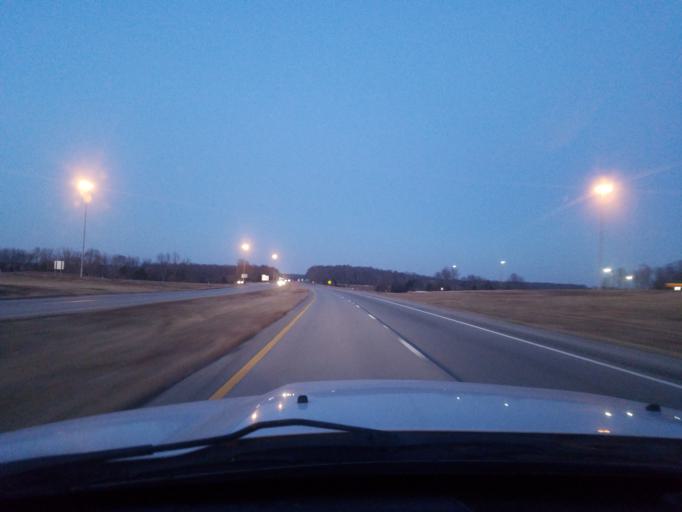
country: US
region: Kentucky
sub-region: Hardin County
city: Elizabethtown
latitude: 37.6547
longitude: -85.8892
